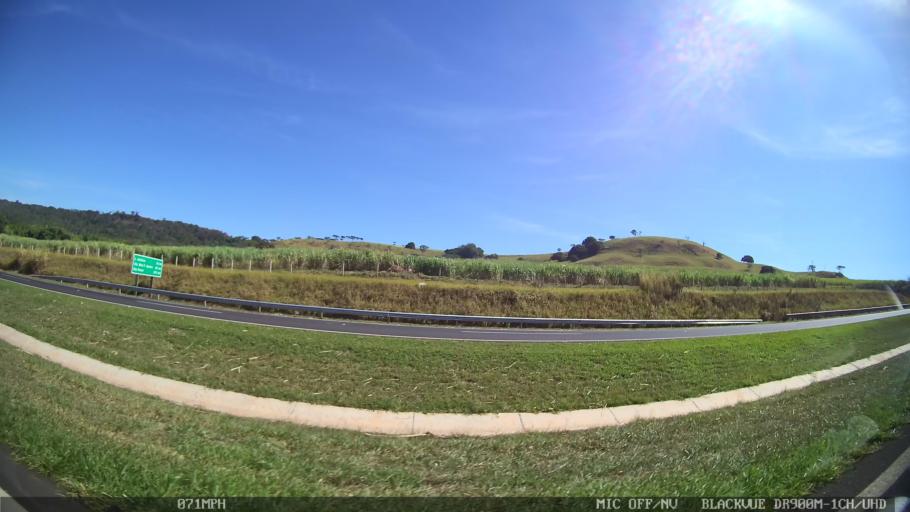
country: BR
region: Sao Paulo
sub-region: Sao Simao
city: Sao Simao
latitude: -21.4811
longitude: -47.6407
